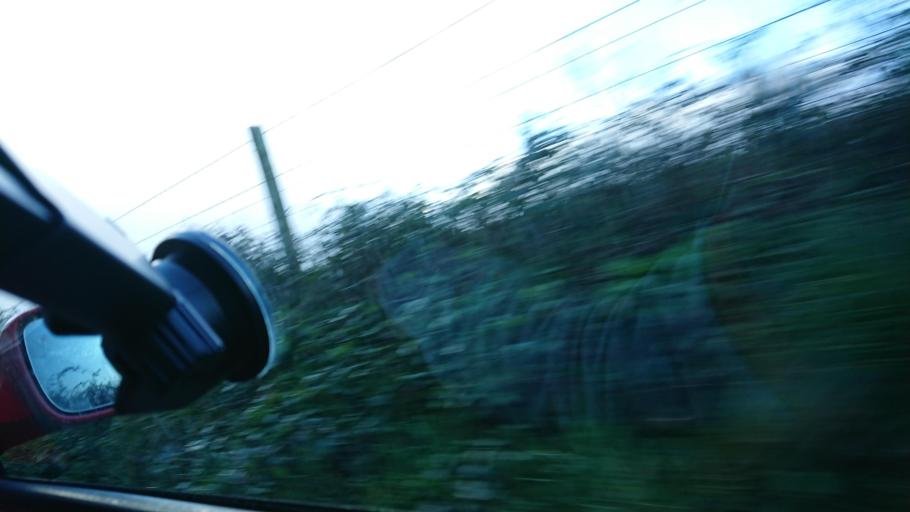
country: GB
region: England
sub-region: Cornwall
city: Looe
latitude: 50.3414
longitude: -4.4809
